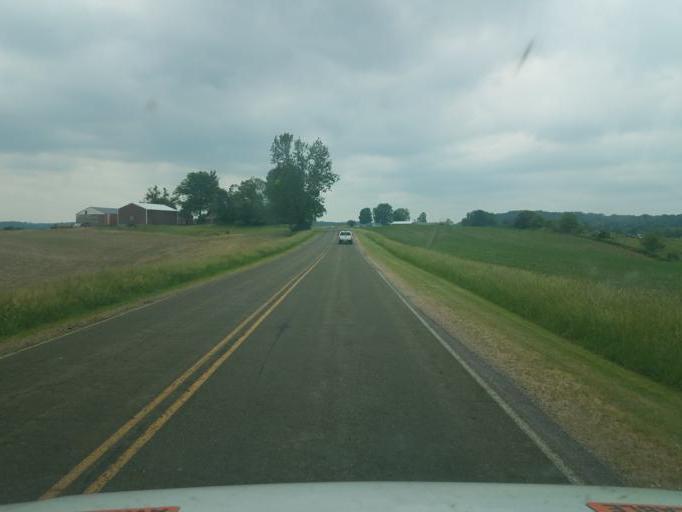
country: US
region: Wisconsin
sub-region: Vernon County
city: Hillsboro
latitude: 43.6471
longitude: -90.2686
